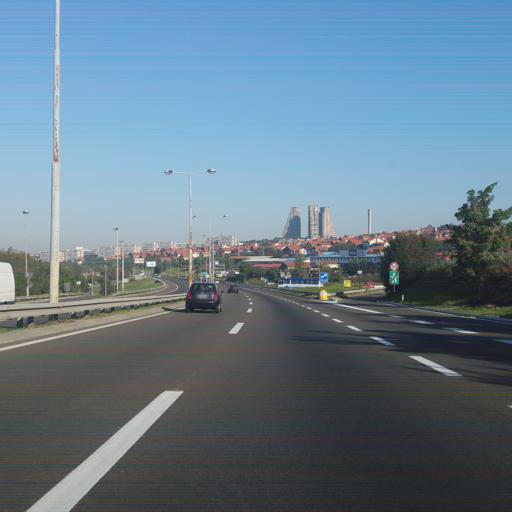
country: RS
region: Central Serbia
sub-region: Belgrade
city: Zvezdara
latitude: 44.7699
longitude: 20.5219
